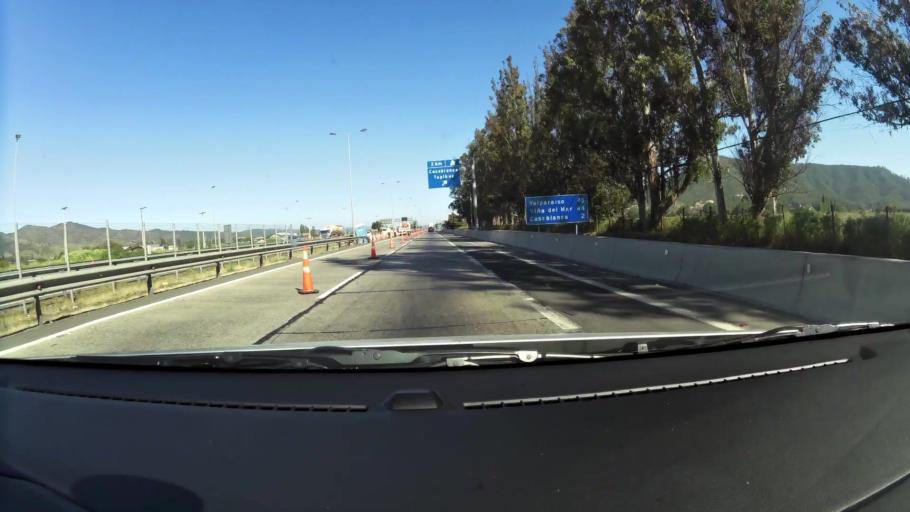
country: CL
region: Valparaiso
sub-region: Provincia de Marga Marga
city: Villa Alemana
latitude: -33.3401
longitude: -71.3674
